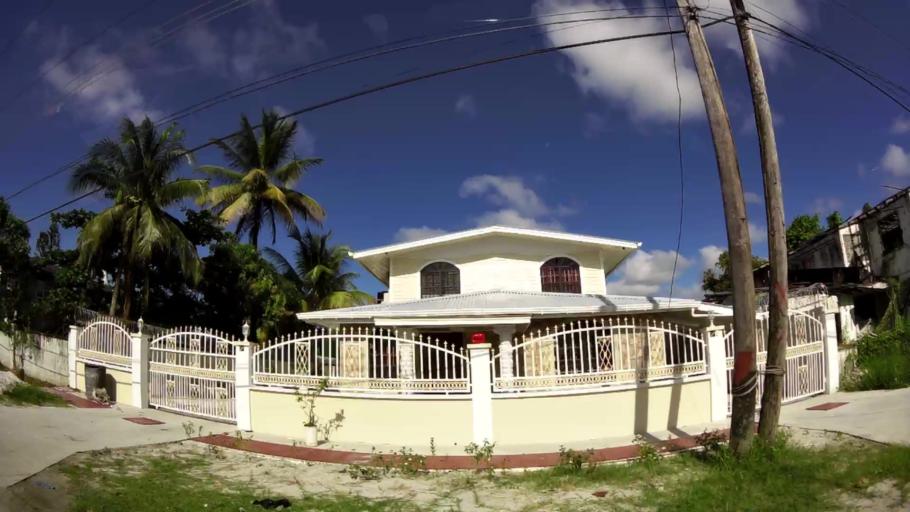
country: GY
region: Demerara-Mahaica
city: Georgetown
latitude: 6.8186
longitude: -58.1304
